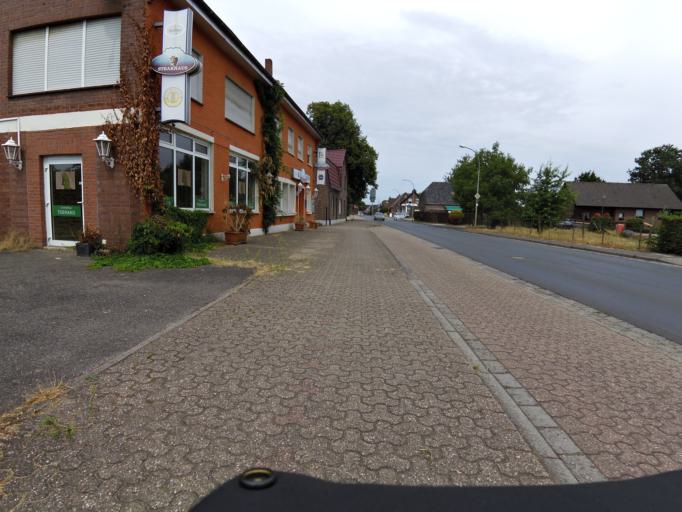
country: DE
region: North Rhine-Westphalia
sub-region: Regierungsbezirk Dusseldorf
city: Weeze
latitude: 51.5880
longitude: 6.1766
